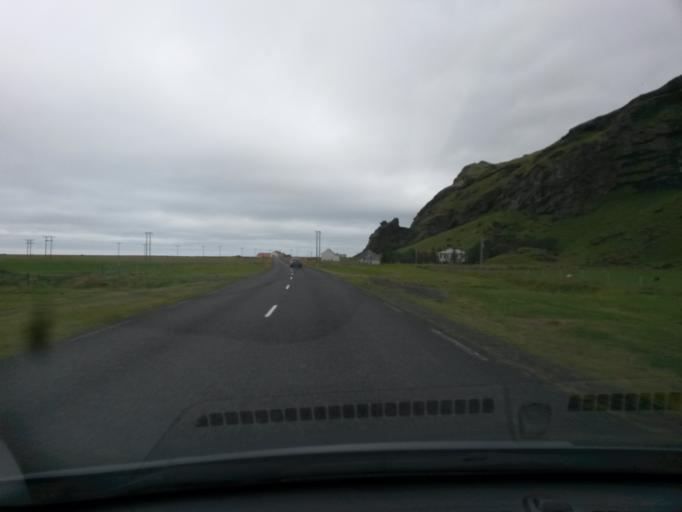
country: IS
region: South
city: Vestmannaeyjar
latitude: 63.5231
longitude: -19.5634
